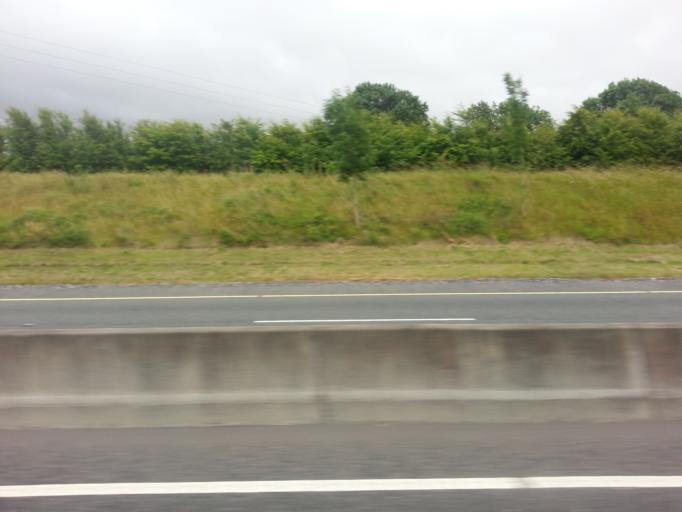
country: IE
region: Leinster
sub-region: Kildare
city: Castledermot
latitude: 52.8351
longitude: -6.8468
